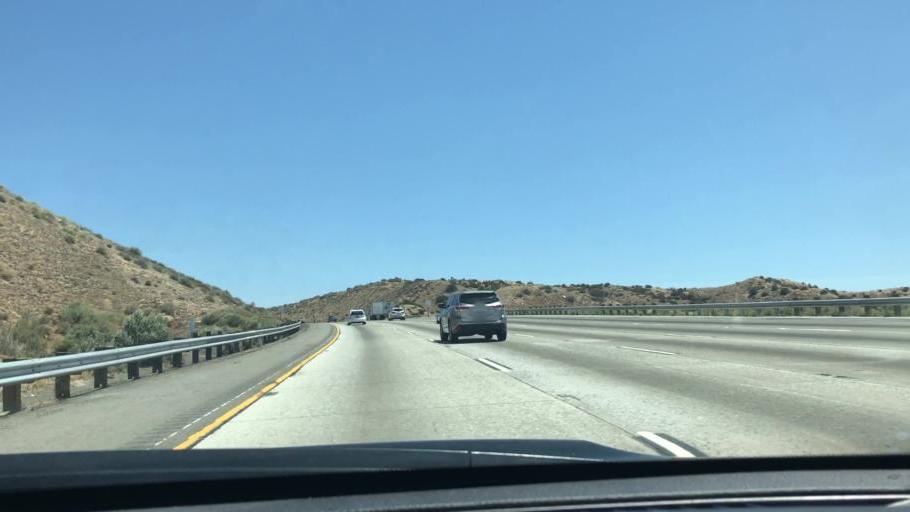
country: US
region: California
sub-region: San Bernardino County
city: Oak Hills
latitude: 34.3474
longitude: -117.4415
